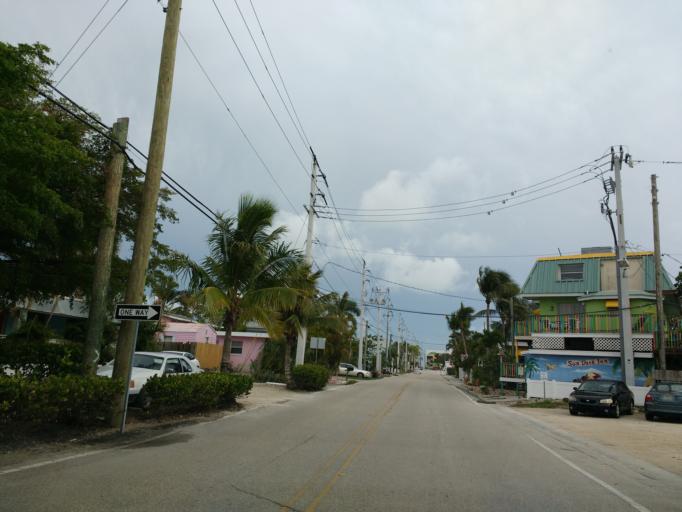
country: US
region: Florida
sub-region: Lee County
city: Fort Myers Beach
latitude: 26.4554
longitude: -81.9539
